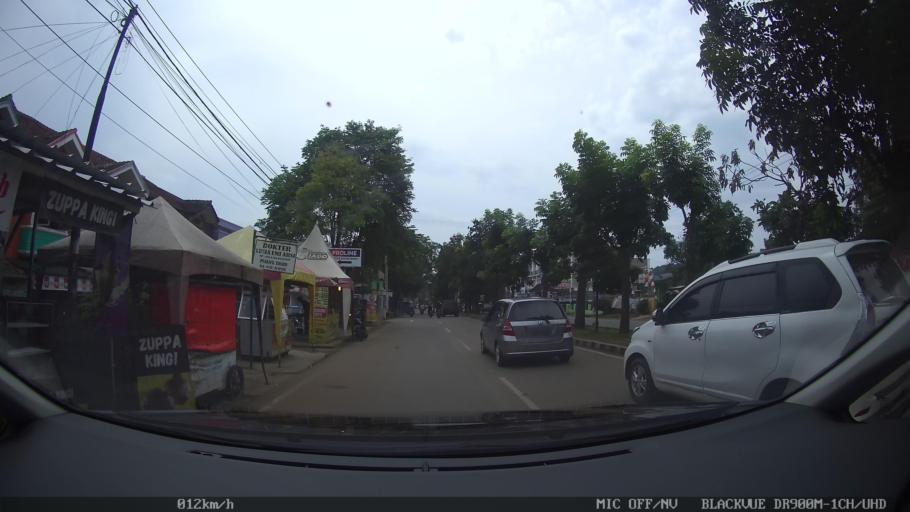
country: ID
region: Lampung
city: Kedaton
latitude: -5.3995
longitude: 105.2091
